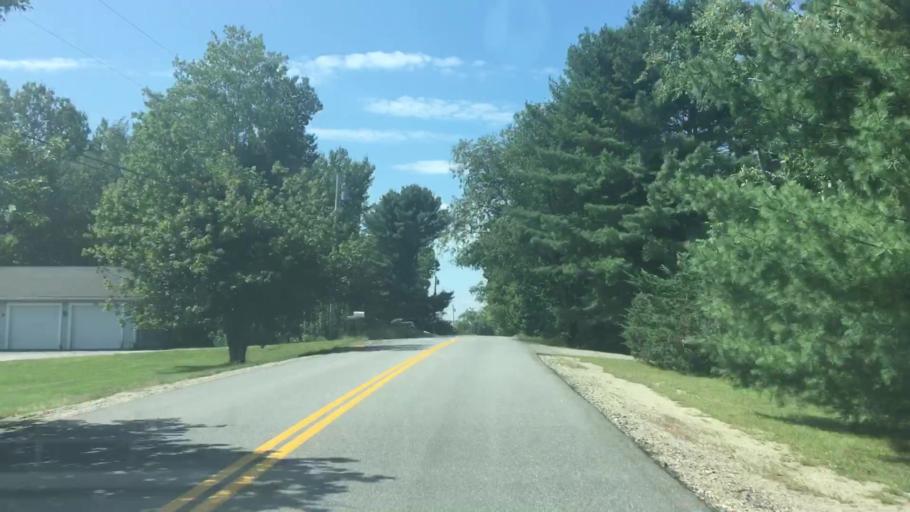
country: US
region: Maine
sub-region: Androscoggin County
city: Lisbon
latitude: 44.0544
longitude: -70.1028
